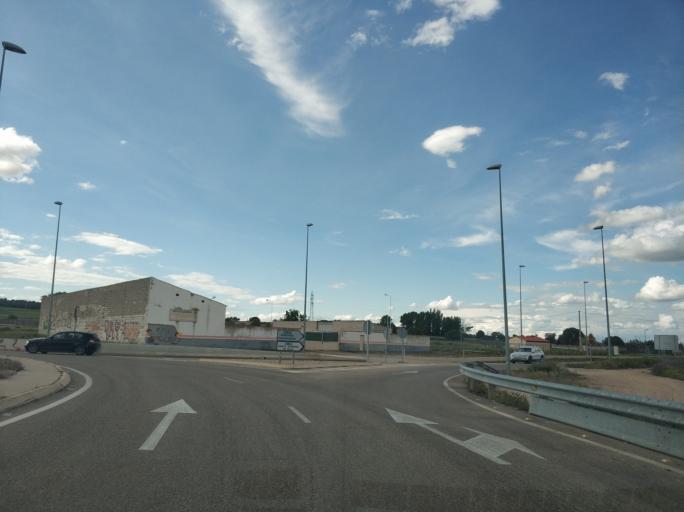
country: ES
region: Castille and Leon
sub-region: Provincia de Burgos
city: Aranda de Duero
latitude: 41.6918
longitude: -3.6689
